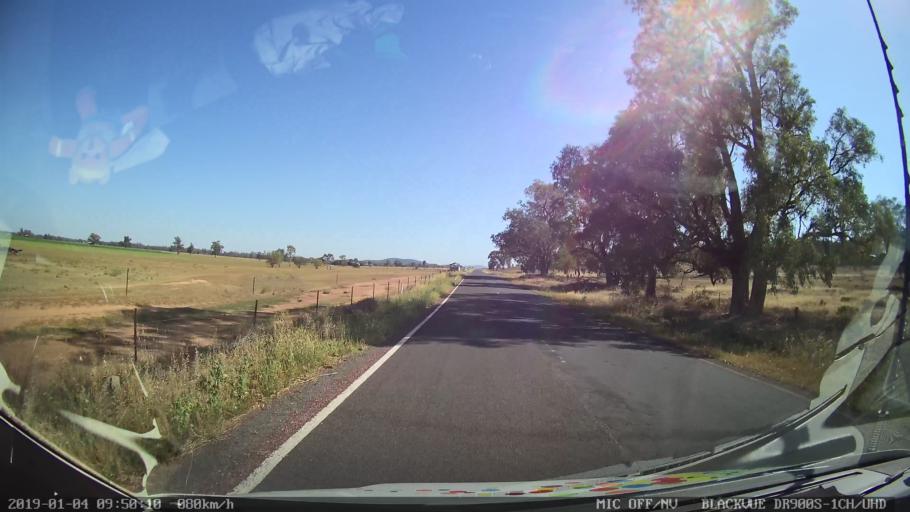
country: AU
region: New South Wales
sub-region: Cabonne
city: Canowindra
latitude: -33.5874
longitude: 148.4148
